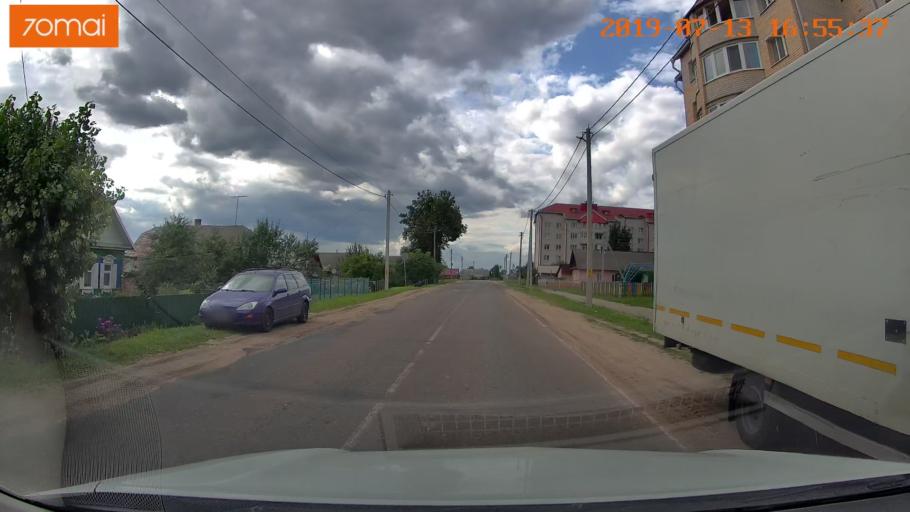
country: BY
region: Mogilev
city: Kirawsk
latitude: 53.2685
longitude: 29.4657
